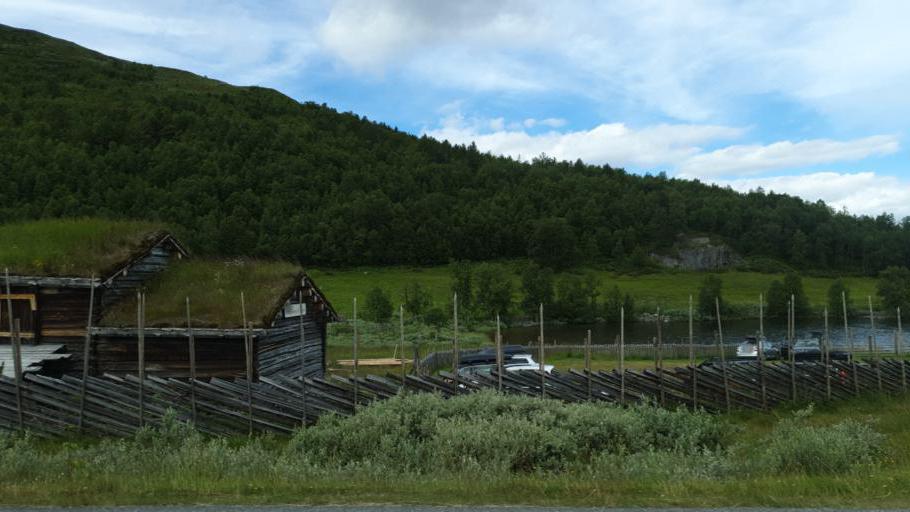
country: NO
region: Oppland
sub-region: Vaga
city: Vagamo
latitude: 61.7586
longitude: 9.0713
